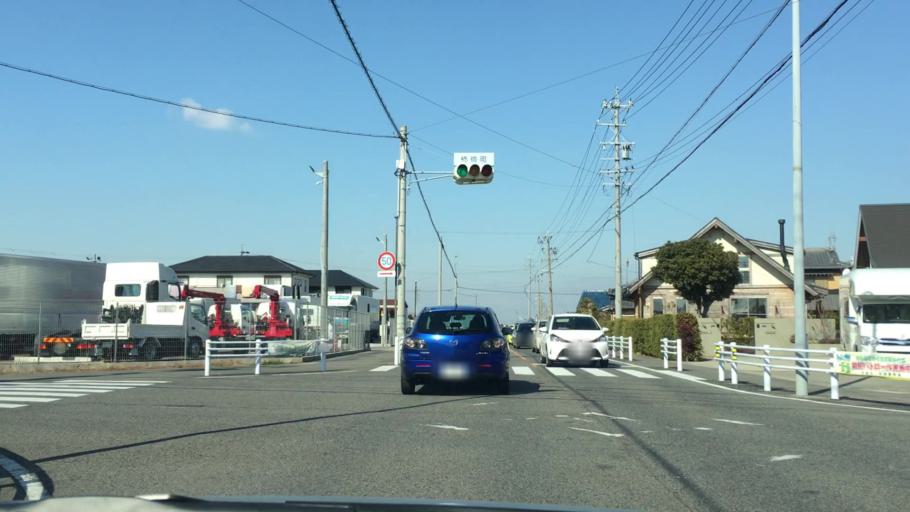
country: JP
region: Aichi
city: Anjo
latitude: 34.9762
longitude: 137.1199
